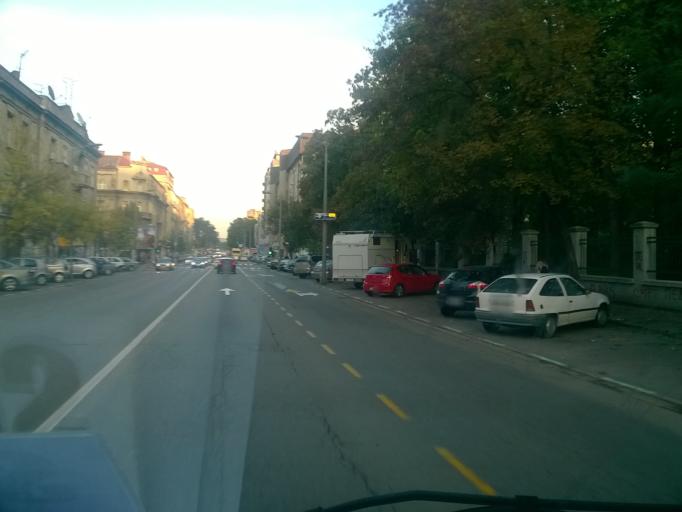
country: RS
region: Central Serbia
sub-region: Belgrade
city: Stari Grad
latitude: 44.8170
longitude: 20.4735
